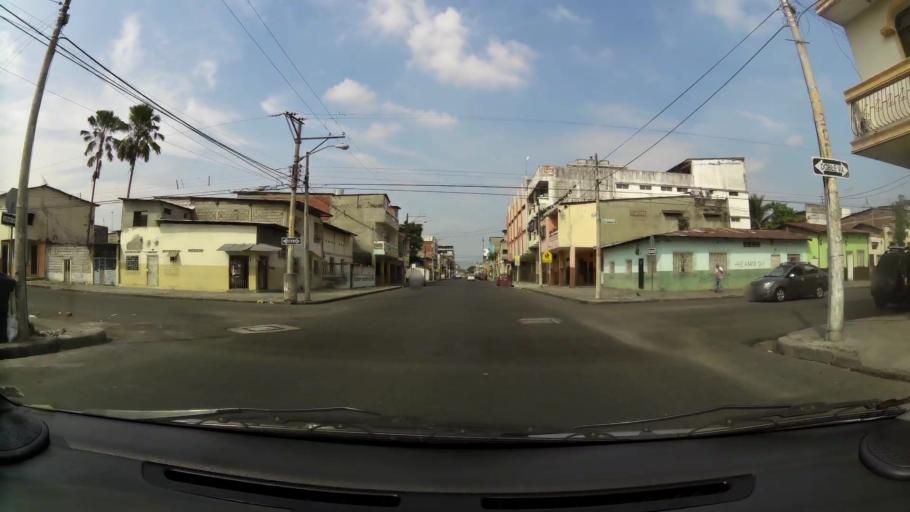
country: EC
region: Guayas
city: Guayaquil
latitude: -2.2083
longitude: -79.9029
